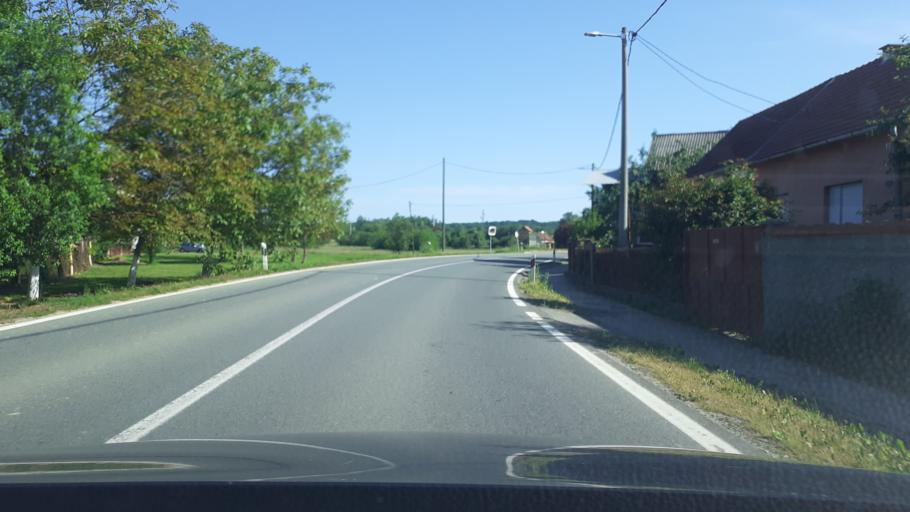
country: HR
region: Brodsko-Posavska
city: Batrina
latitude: 45.1938
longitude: 17.6627
